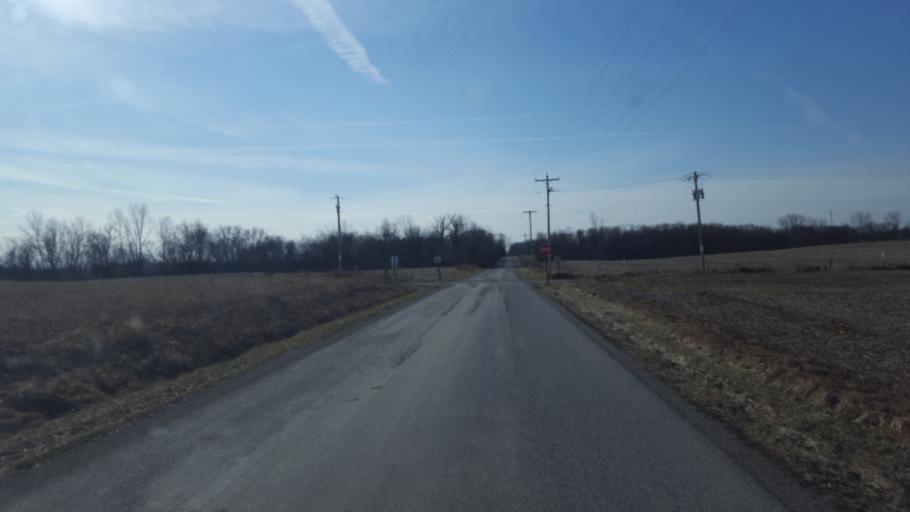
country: US
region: Ohio
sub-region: Morrow County
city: Mount Gilead
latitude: 40.5740
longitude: -82.7575
